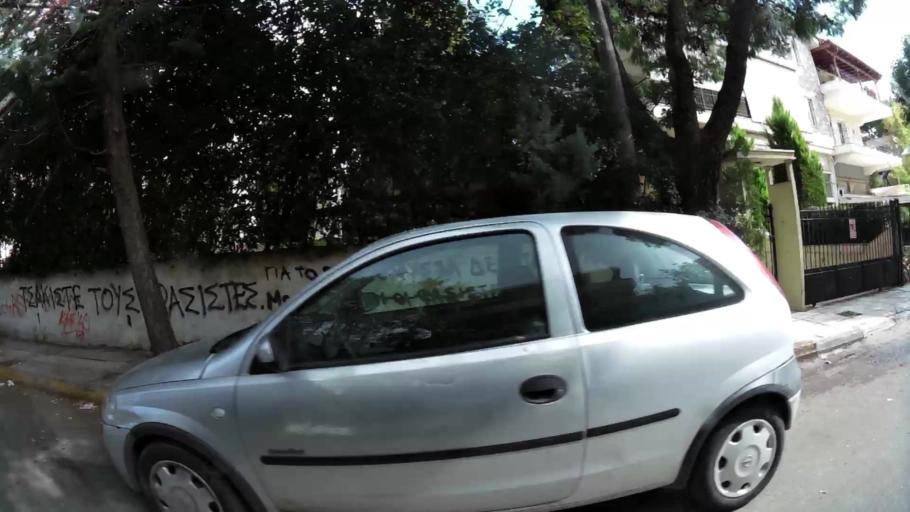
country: GR
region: Attica
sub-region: Nomarchia Athinas
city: Melissia
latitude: 38.0566
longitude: 23.8390
